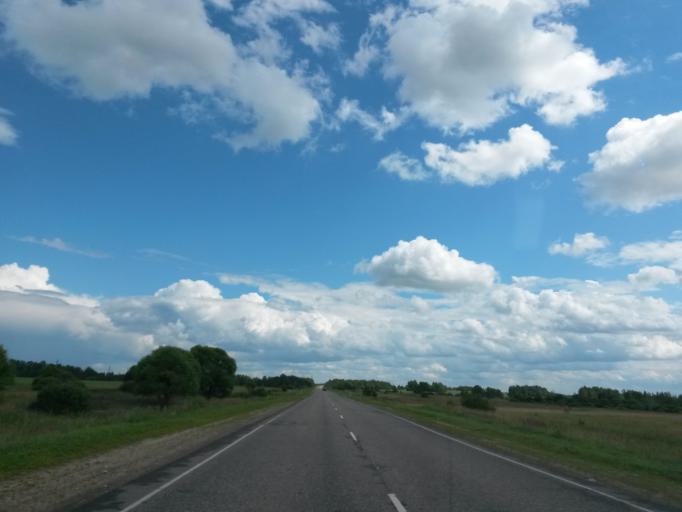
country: RU
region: Ivanovo
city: Pistsovo
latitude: 57.1894
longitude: 40.4291
